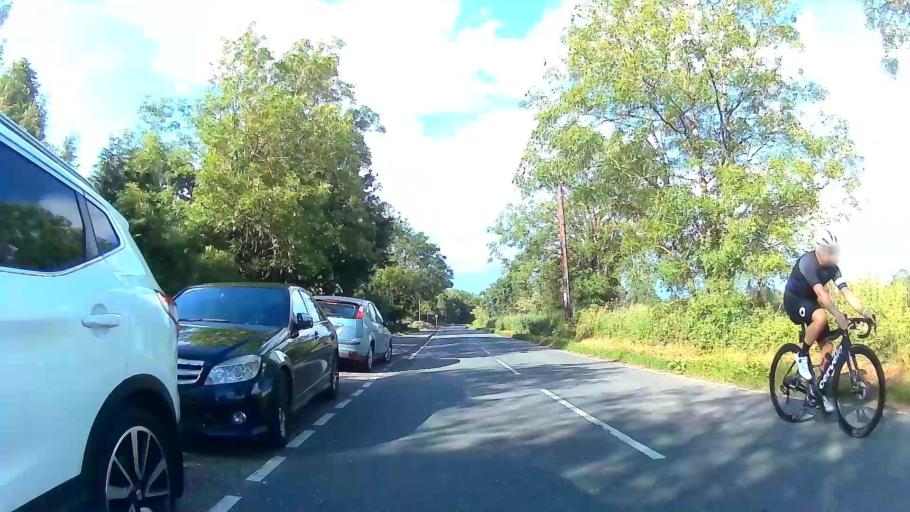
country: GB
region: England
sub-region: Essex
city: Kelvedon Hatch
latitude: 51.6923
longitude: 0.3217
